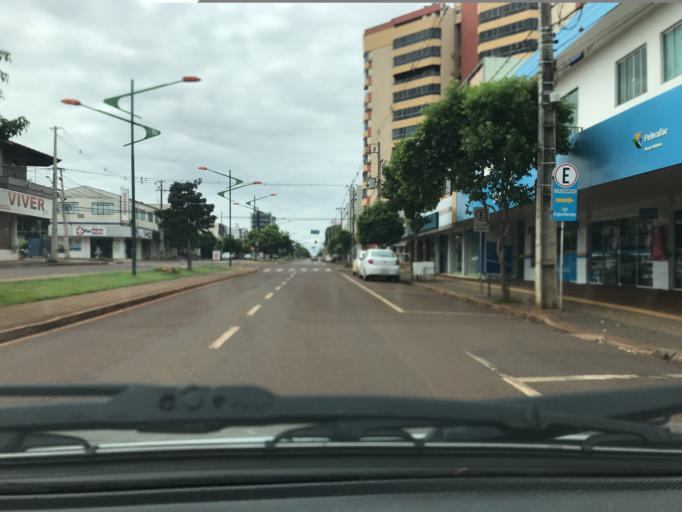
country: BR
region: Parana
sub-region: Palotina
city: Palotina
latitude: -24.2806
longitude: -53.8410
